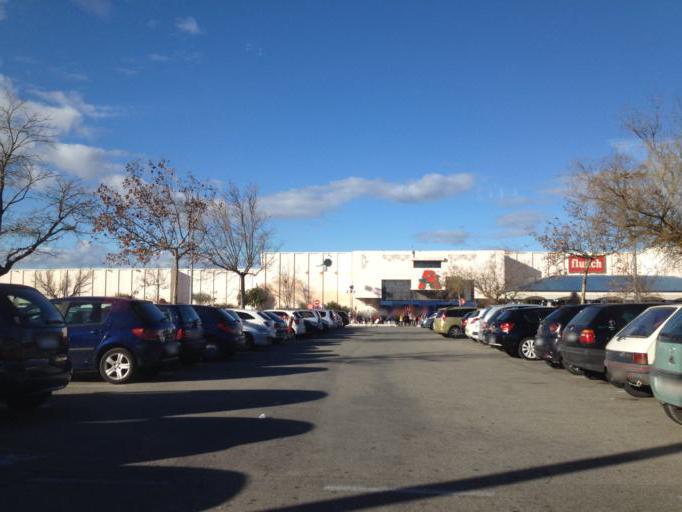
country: FR
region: Provence-Alpes-Cote d'Azur
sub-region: Departement du Vaucluse
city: Vedene
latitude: 43.9814
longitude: 4.8822
